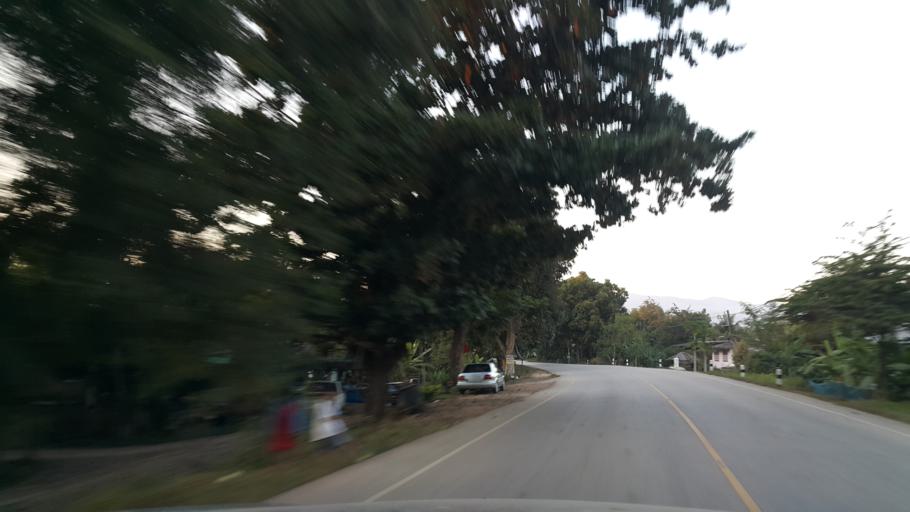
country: TH
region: Phrae
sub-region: Amphoe Wang Chin
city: Wang Chin
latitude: 17.8684
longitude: 99.6216
